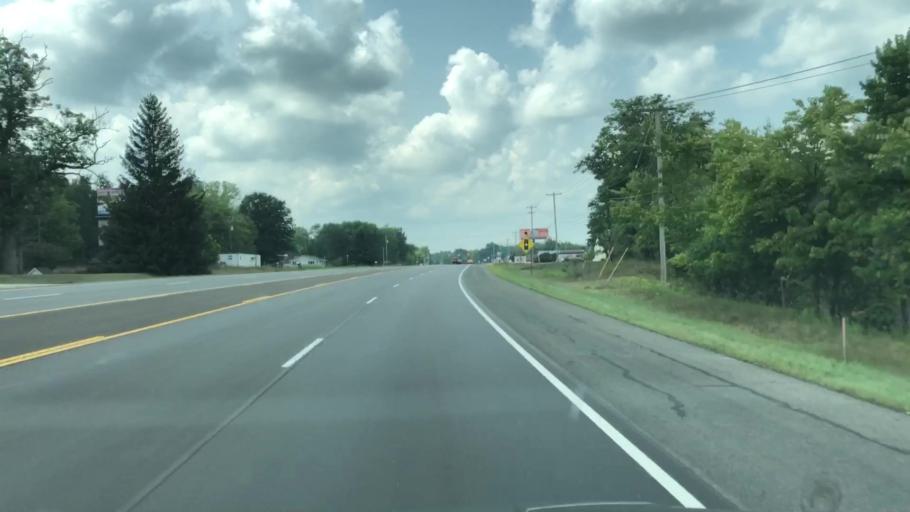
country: US
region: Michigan
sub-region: Isabella County
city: Shepherd
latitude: 43.6102
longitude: -84.5825
